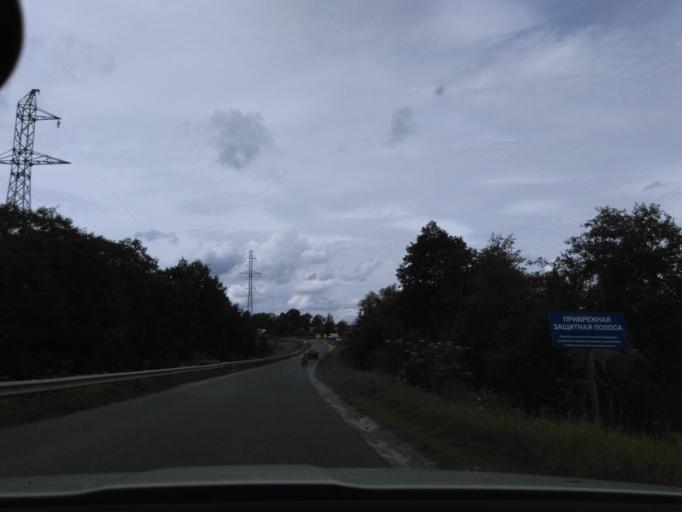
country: RU
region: Tverskaya
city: Konakovo
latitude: 56.6682
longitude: 36.7171
